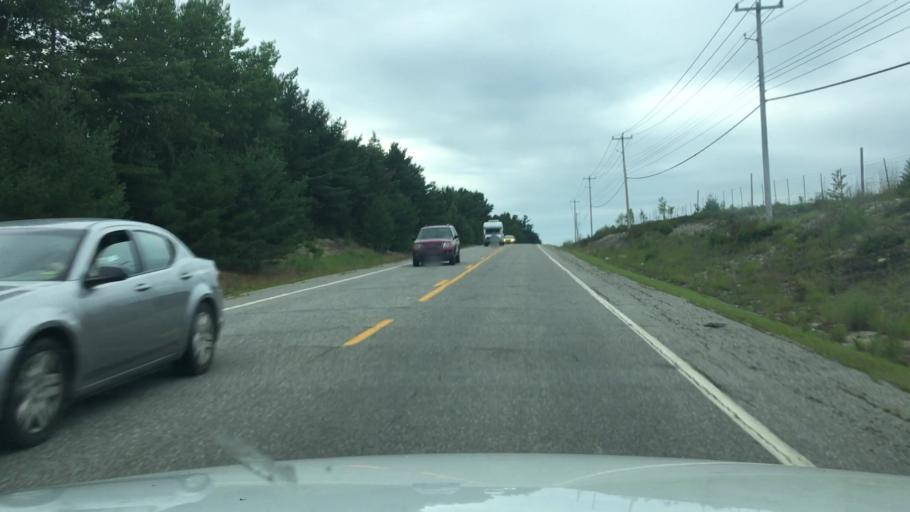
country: US
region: Maine
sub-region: Washington County
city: Addison
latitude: 44.6409
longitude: -67.6396
